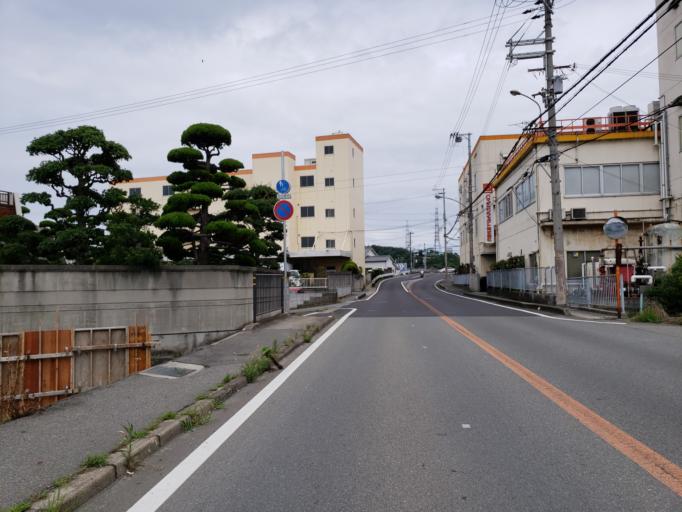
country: JP
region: Hyogo
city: Himeji
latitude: 34.7917
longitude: 134.6886
